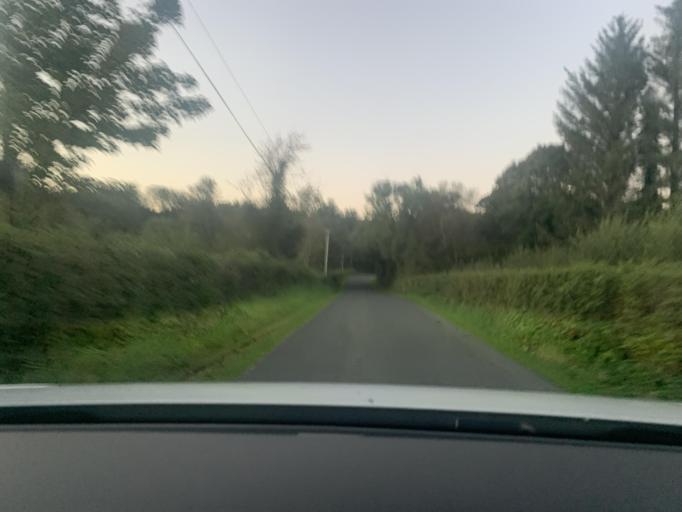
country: IE
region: Connaught
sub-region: County Leitrim
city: Manorhamilton
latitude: 54.2555
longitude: -8.3049
